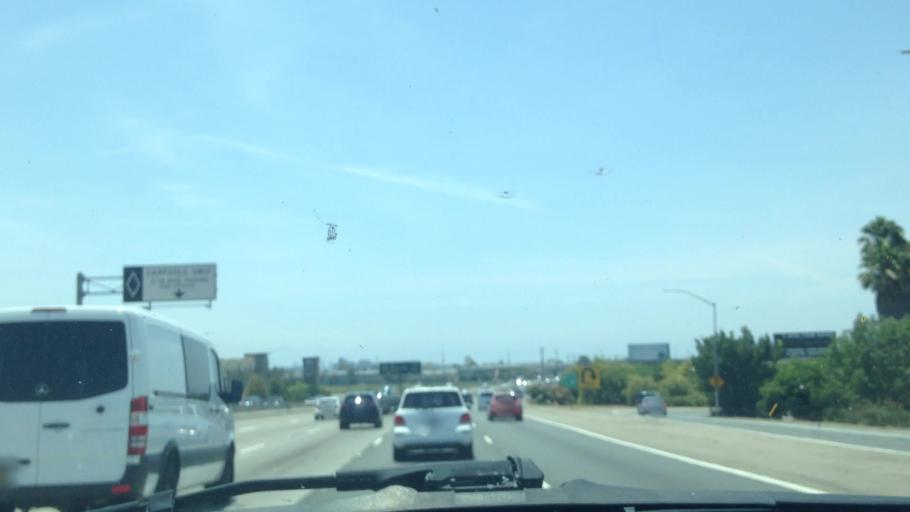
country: US
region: California
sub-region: Orange County
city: Tustin
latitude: 33.7265
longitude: -117.8352
